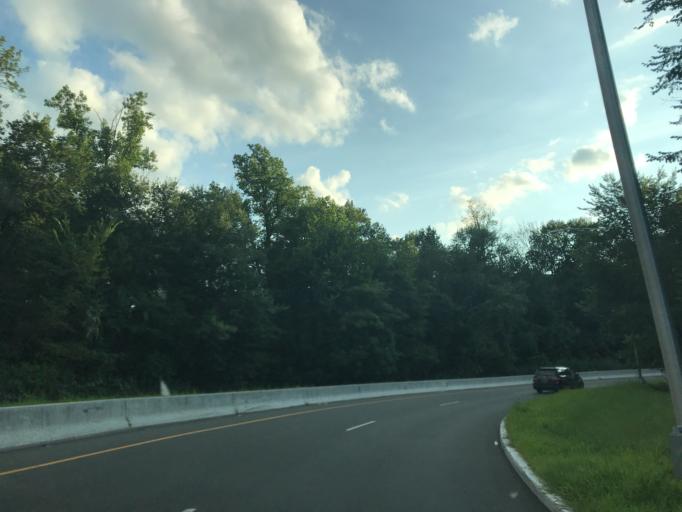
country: US
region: New Jersey
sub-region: Morris County
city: Parsippany
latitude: 40.8372
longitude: -74.4515
